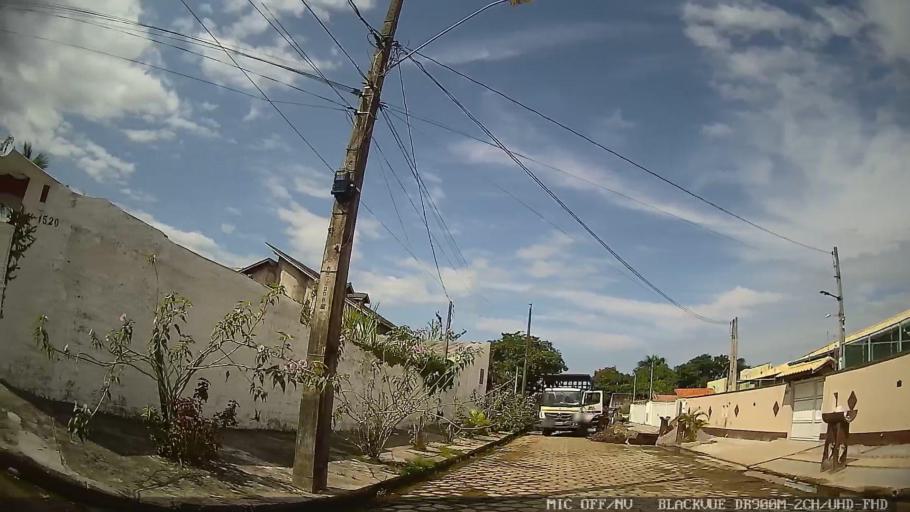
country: BR
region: Sao Paulo
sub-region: Itanhaem
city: Itanhaem
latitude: -24.1994
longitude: -46.8411
